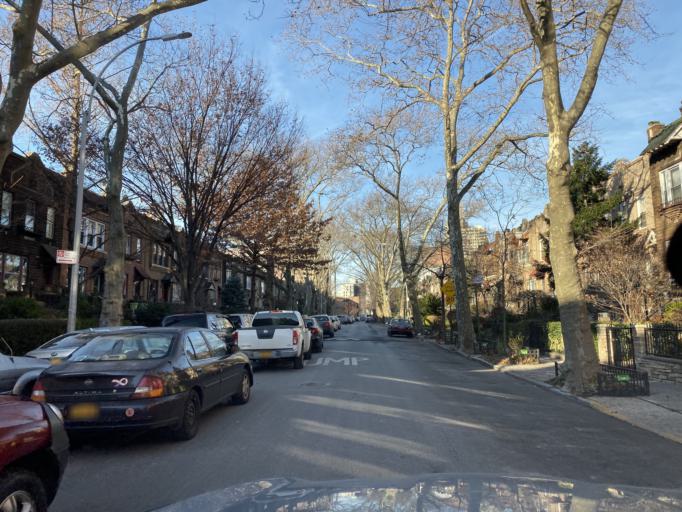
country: US
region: New York
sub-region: Kings County
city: Brooklyn
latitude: 40.6665
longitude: -73.9540
